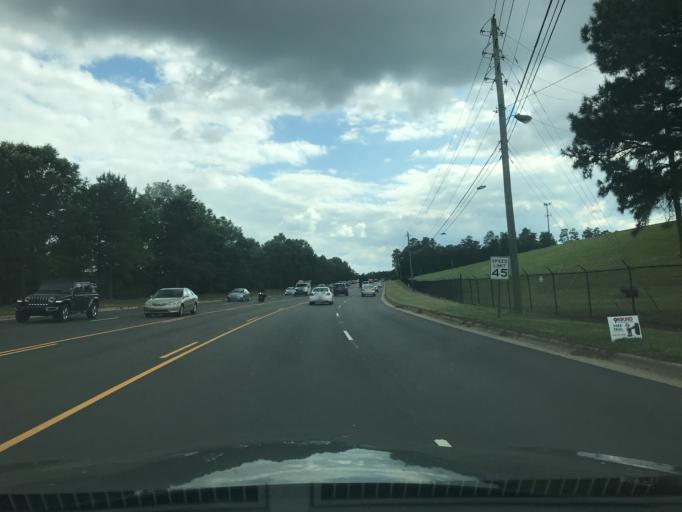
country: US
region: North Carolina
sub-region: Wake County
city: Wake Forest
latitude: 35.9131
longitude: -78.5957
